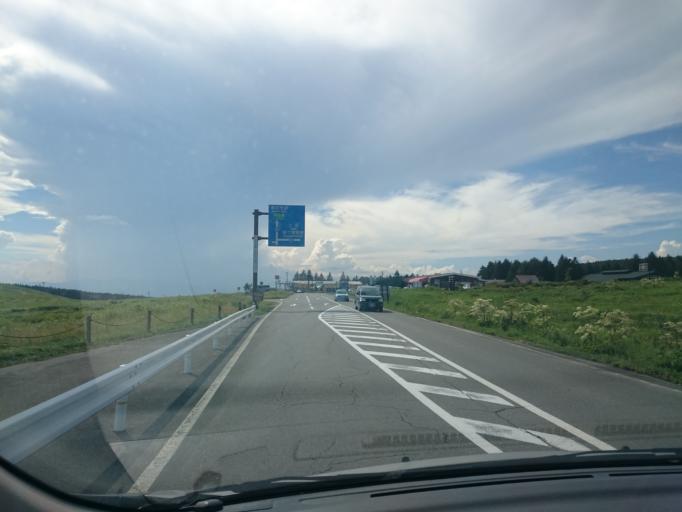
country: JP
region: Nagano
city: Suwa
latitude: 36.0966
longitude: 138.1702
